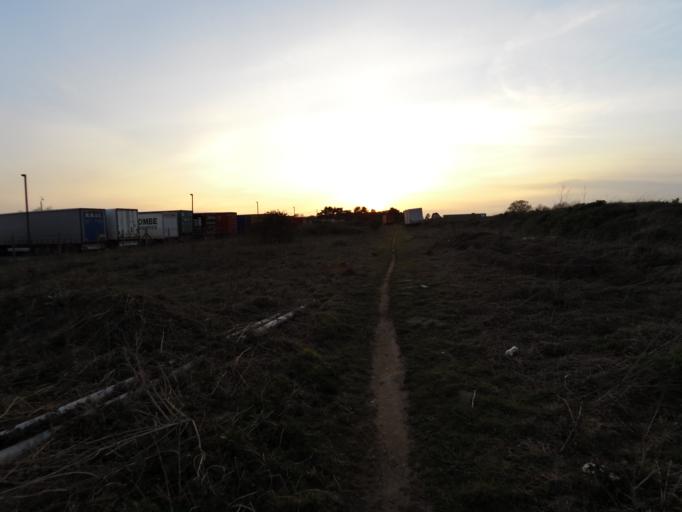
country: GB
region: England
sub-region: Suffolk
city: Kesgrave
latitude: 52.0260
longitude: 1.2258
